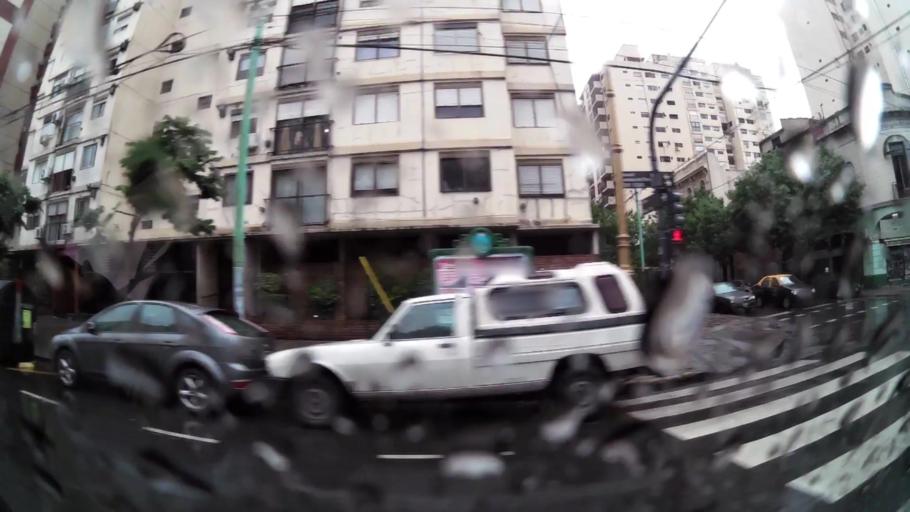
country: AR
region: Buenos Aires
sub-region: Partido de Avellaneda
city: Avellaneda
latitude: -34.6424
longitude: -58.3739
